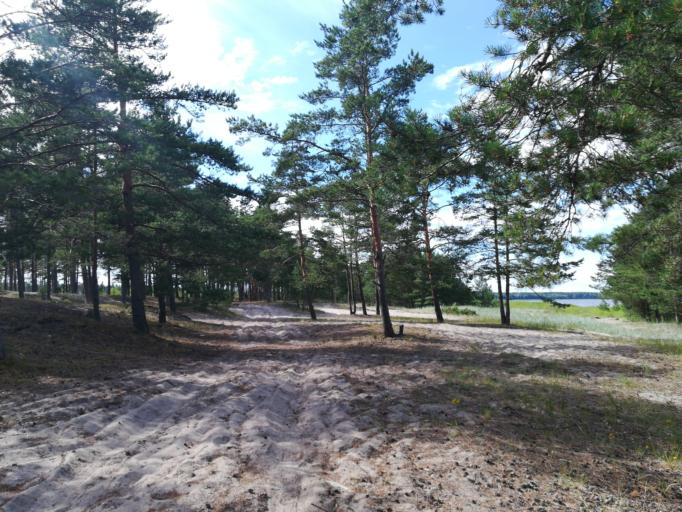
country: RU
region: Leningrad
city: Ust'-Luga
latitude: 59.6818
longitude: 28.2301
